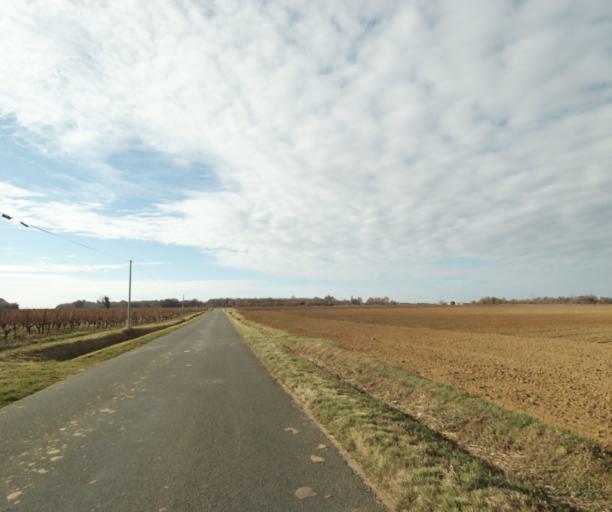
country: FR
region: Poitou-Charentes
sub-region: Departement de la Charente-Maritime
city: Corme-Royal
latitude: 45.7217
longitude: -0.8312
